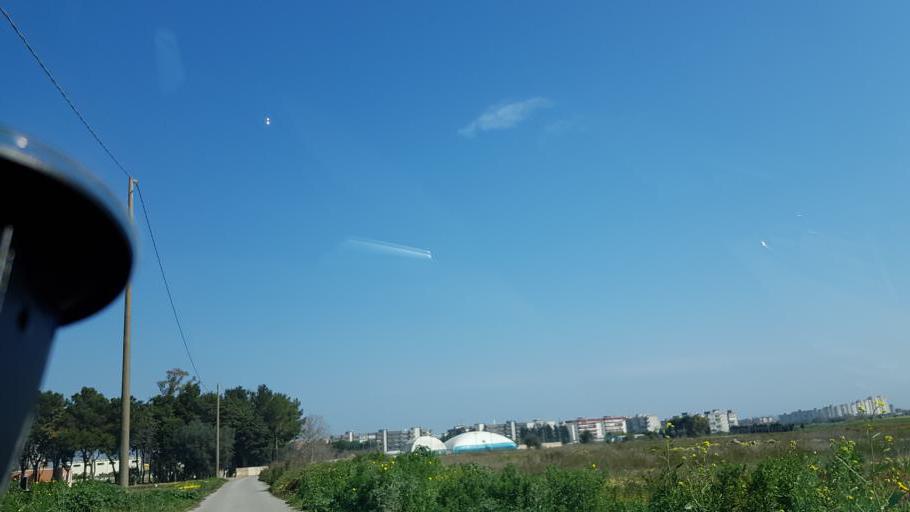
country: IT
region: Apulia
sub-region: Provincia di Brindisi
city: Brindisi
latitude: 40.6126
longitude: 17.9298
